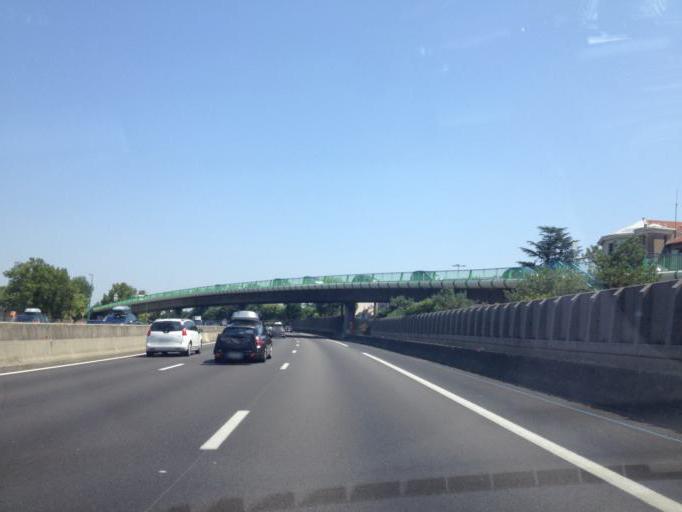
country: FR
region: Rhone-Alpes
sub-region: Departement de la Drome
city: Valence
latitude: 44.9352
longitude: 4.8884
